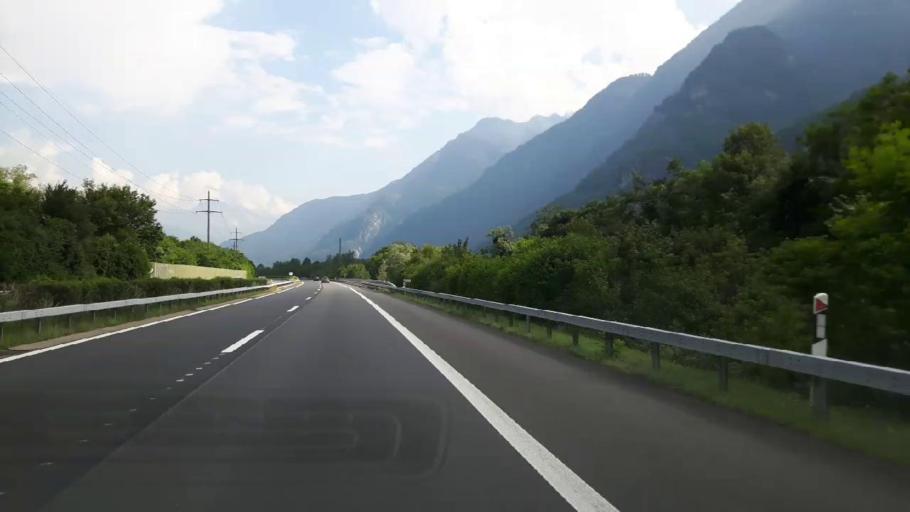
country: CH
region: Ticino
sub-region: Riviera District
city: Lodrino
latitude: 46.3115
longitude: 8.9820
